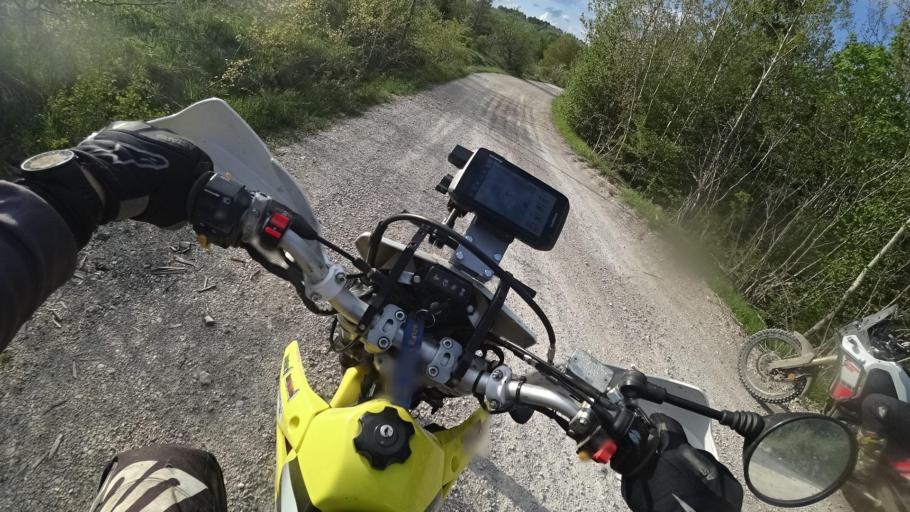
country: BA
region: Federation of Bosnia and Herzegovina
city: Glamoc
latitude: 44.0834
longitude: 16.7365
